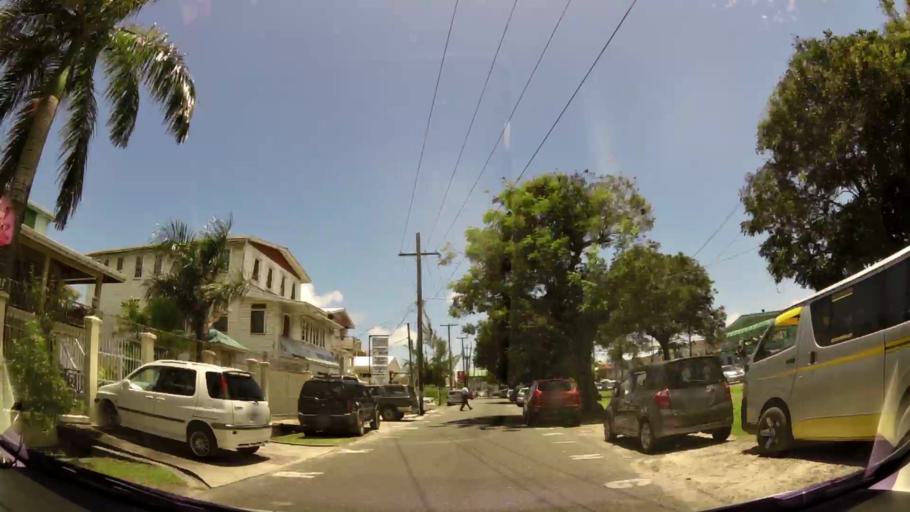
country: GY
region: Demerara-Mahaica
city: Georgetown
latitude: 6.8180
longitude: -58.1623
